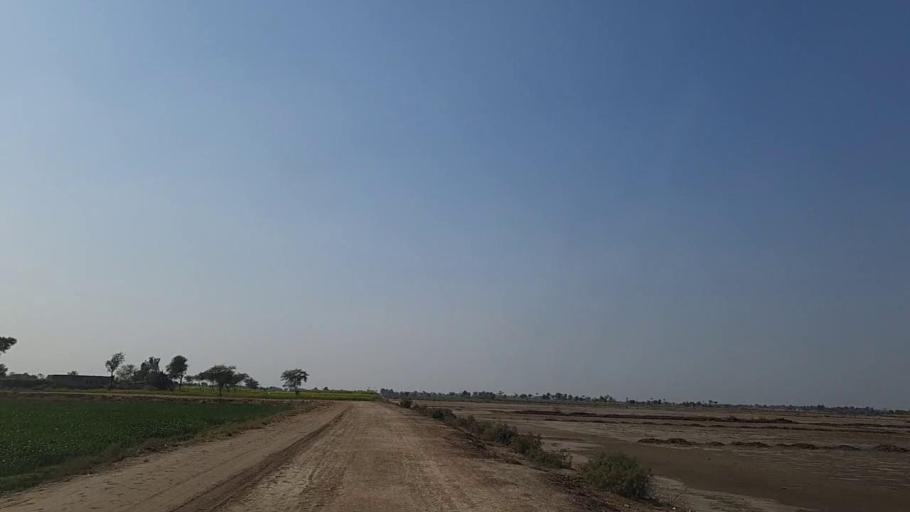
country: PK
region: Sindh
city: Daur
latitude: 26.4533
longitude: 68.2436
